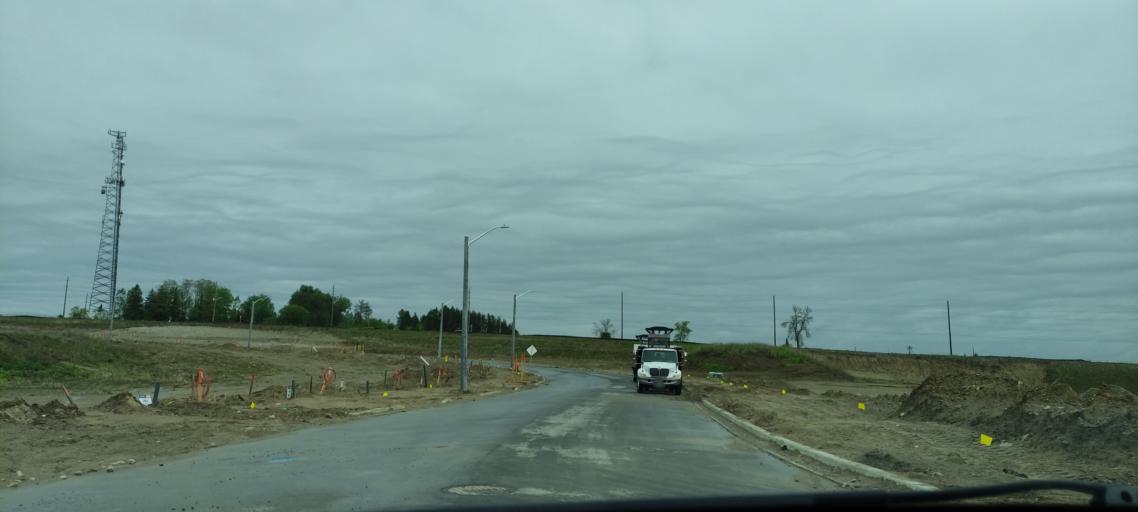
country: CA
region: Ontario
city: Kitchener
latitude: 43.4032
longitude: -80.5388
